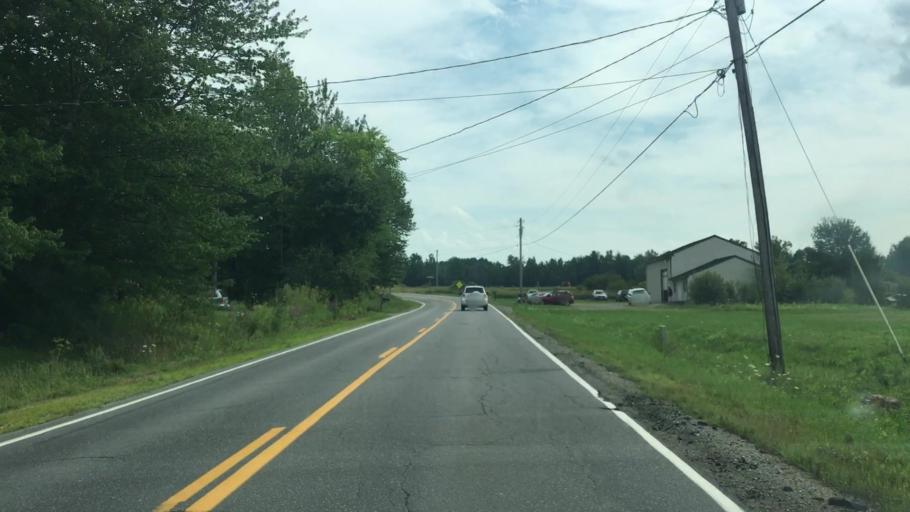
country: US
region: Maine
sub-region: Kennebec County
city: Vassalboro
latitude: 44.4398
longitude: -69.6057
